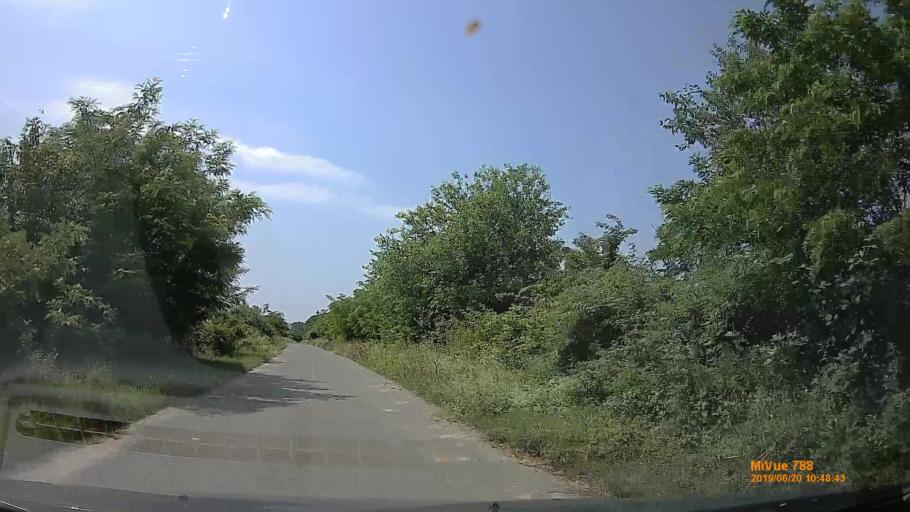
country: HU
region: Baranya
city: Hidas
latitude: 46.1663
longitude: 18.5825
